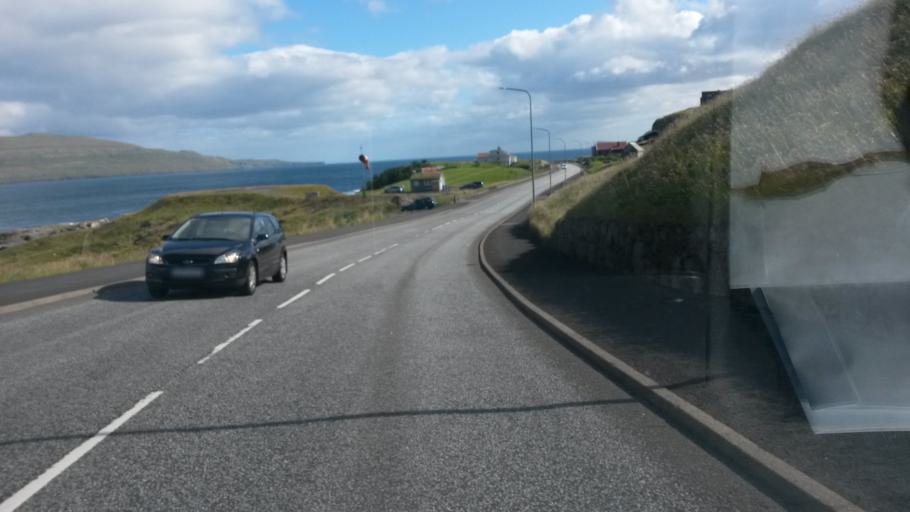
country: FO
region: Streymoy
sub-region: Torshavn
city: Torshavn
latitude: 62.0227
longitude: -6.7593
